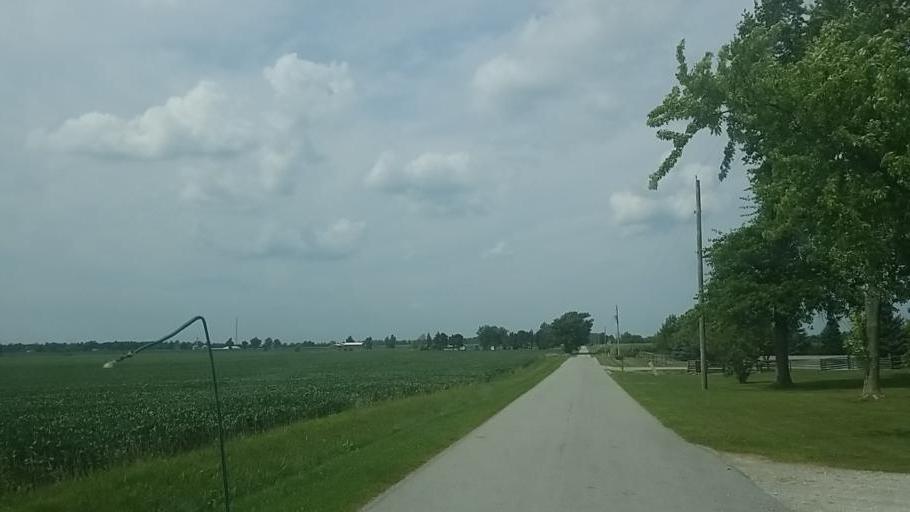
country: US
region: Ohio
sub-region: Hardin County
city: Forest
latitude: 40.8077
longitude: -83.4675
